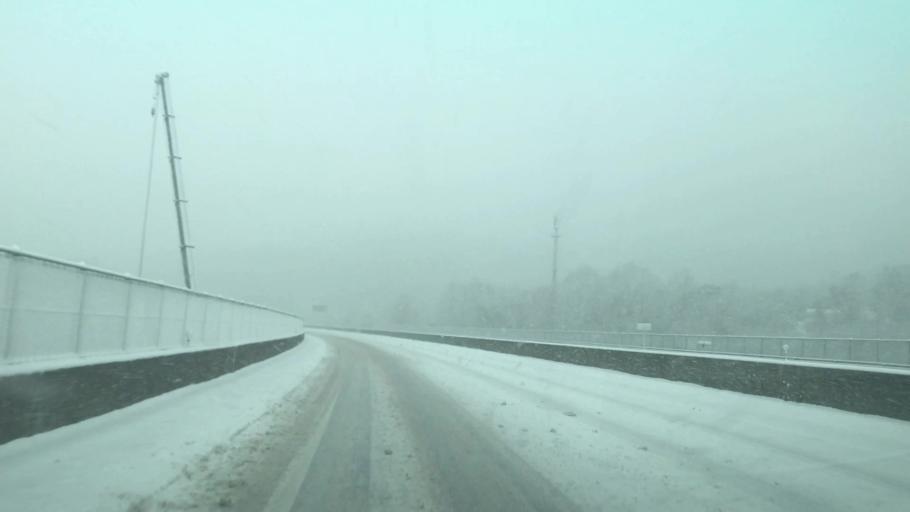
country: JP
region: Hokkaido
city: Muroran
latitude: 42.4177
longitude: 141.0811
